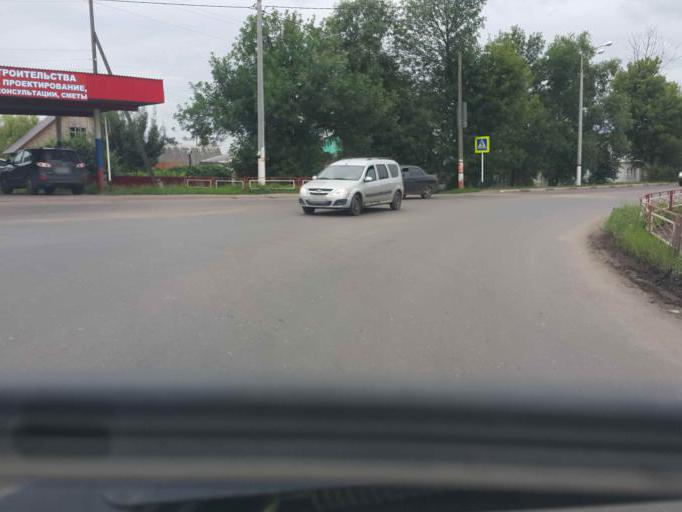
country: RU
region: Tambov
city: Zavoronezhskoye
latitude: 52.8827
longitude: 40.5441
